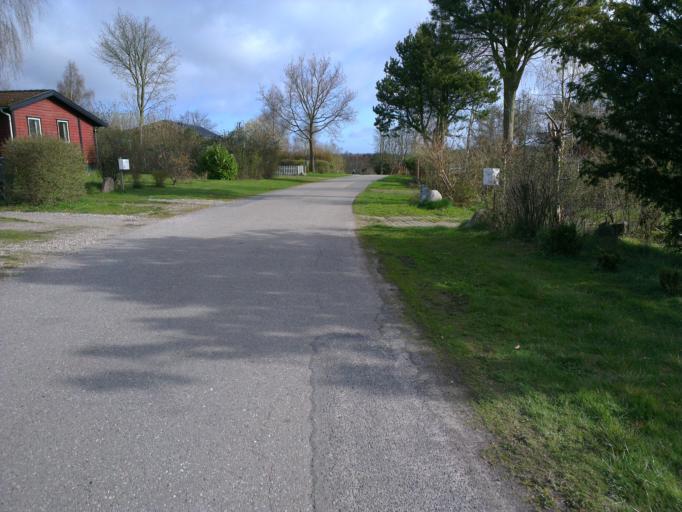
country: DK
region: Capital Region
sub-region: Frederikssund Kommune
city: Jaegerspris
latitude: 55.8334
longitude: 11.9730
